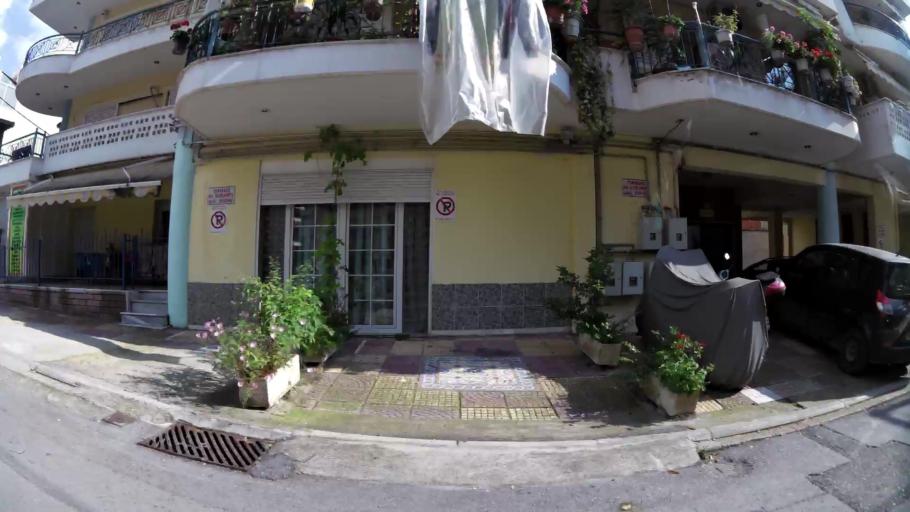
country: GR
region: Central Macedonia
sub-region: Nomos Thessalonikis
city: Sykies
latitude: 40.6557
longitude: 22.9552
